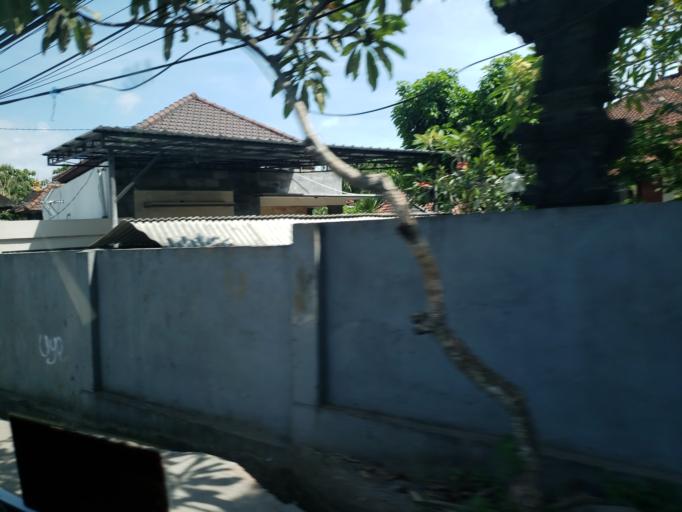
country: ID
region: Bali
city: Kangin
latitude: -8.8207
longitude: 115.1486
